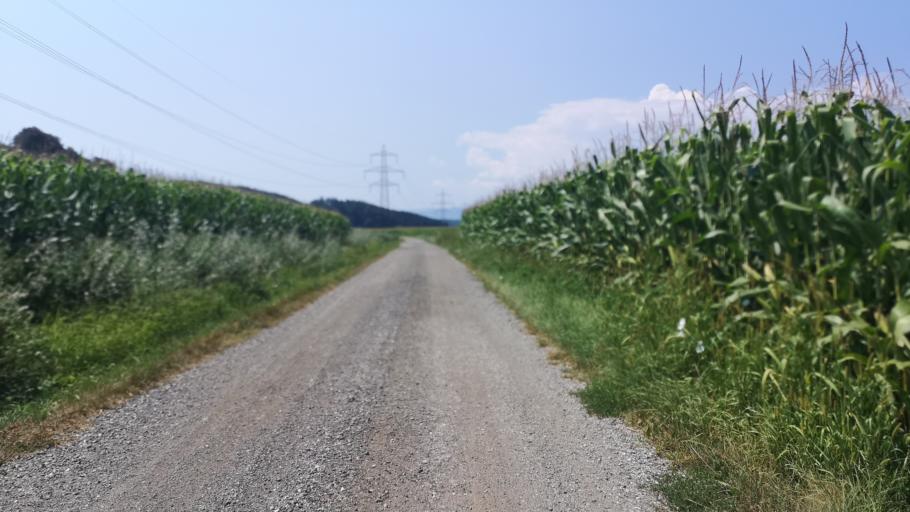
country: AT
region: Styria
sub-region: Politischer Bezirk Deutschlandsberg
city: Wettmannstatten
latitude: 46.8278
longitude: 15.3667
